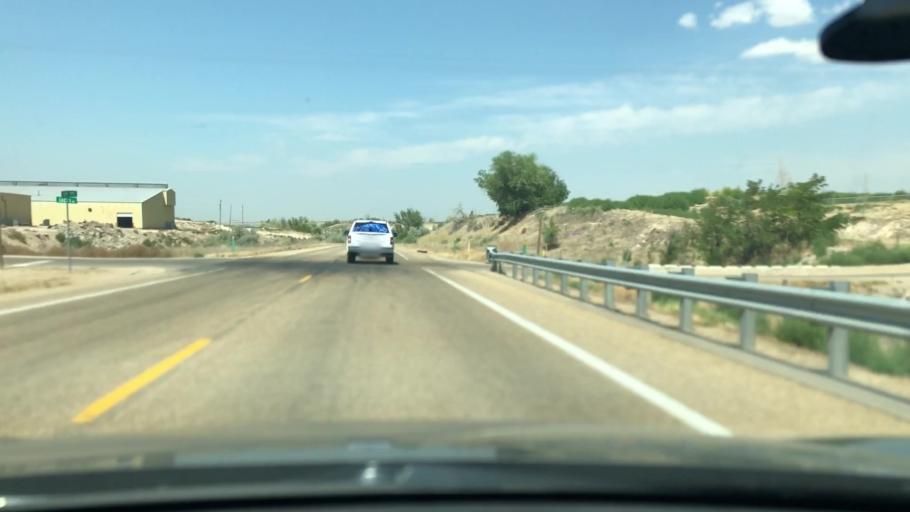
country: US
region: Idaho
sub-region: Canyon County
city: Wilder
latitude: 43.7123
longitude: -116.9118
